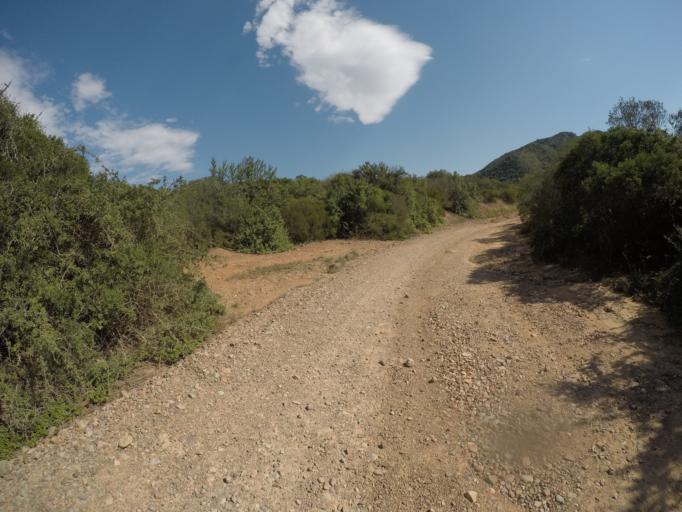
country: ZA
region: Eastern Cape
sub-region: Cacadu District Municipality
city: Kareedouw
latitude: -33.6555
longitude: 24.4103
